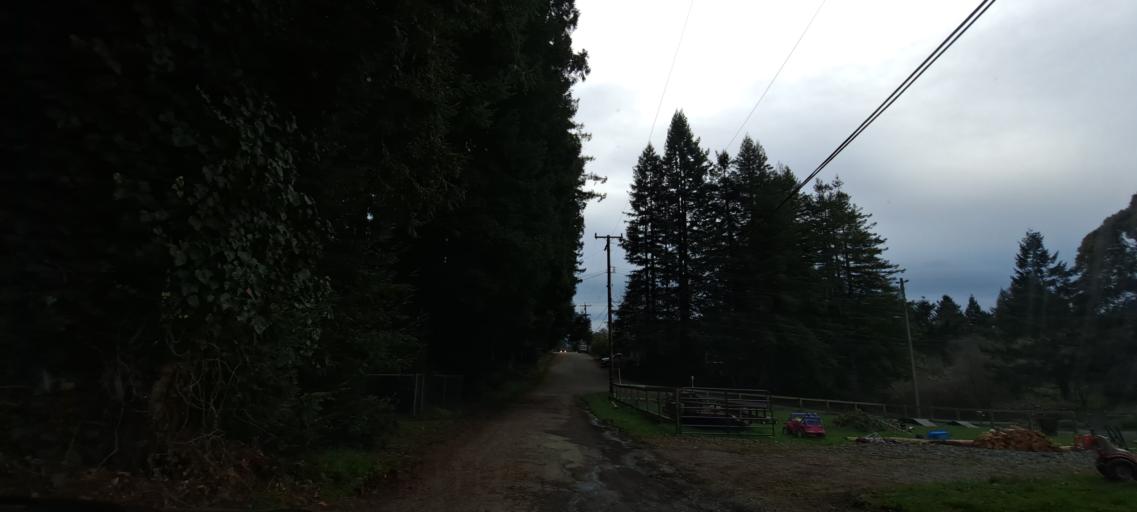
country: US
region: California
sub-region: Humboldt County
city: Fortuna
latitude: 40.6066
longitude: -124.1543
